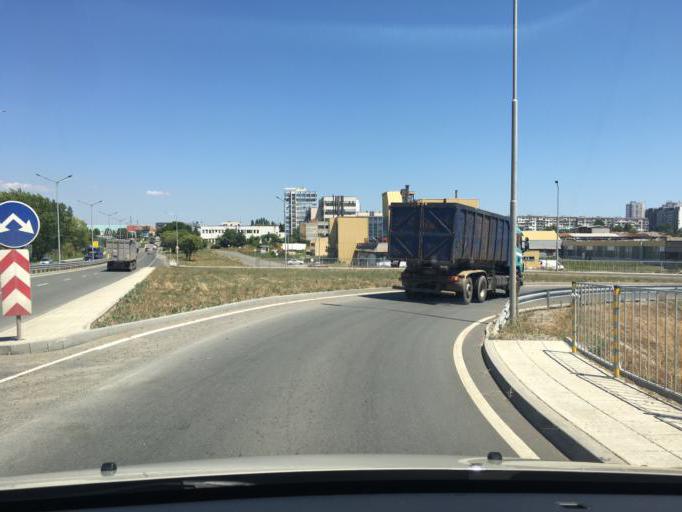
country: BG
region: Burgas
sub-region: Obshtina Burgas
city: Burgas
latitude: 42.5164
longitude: 27.4371
